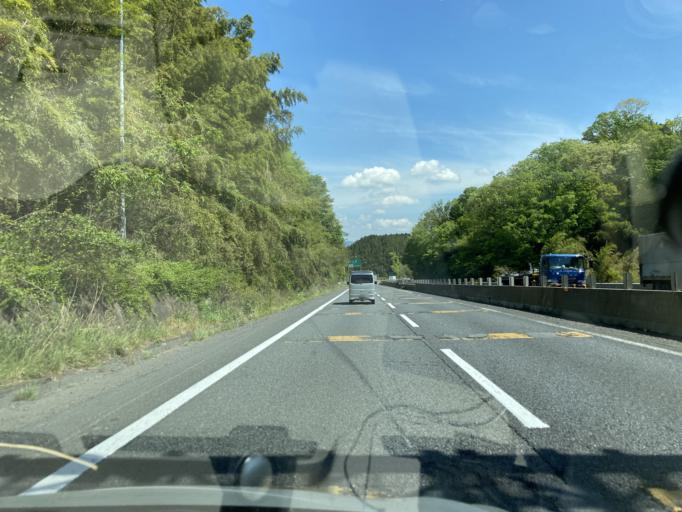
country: JP
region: Mie
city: Nabari
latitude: 34.6750
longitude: 136.0339
